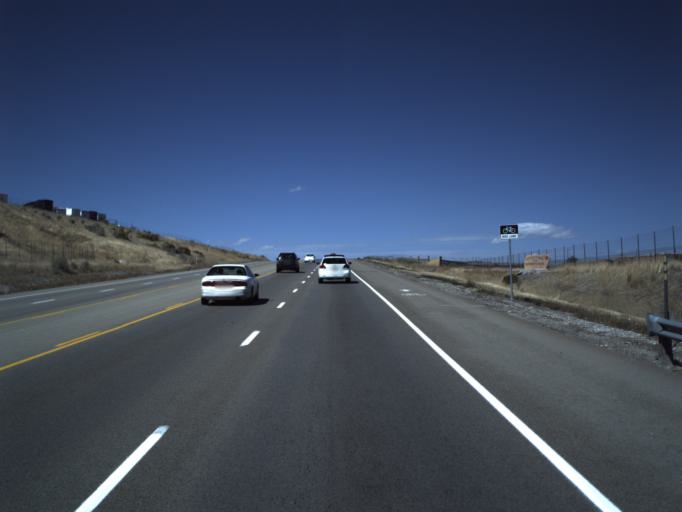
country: US
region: Utah
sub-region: Salt Lake County
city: Bluffdale
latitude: 40.4272
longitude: -111.9271
